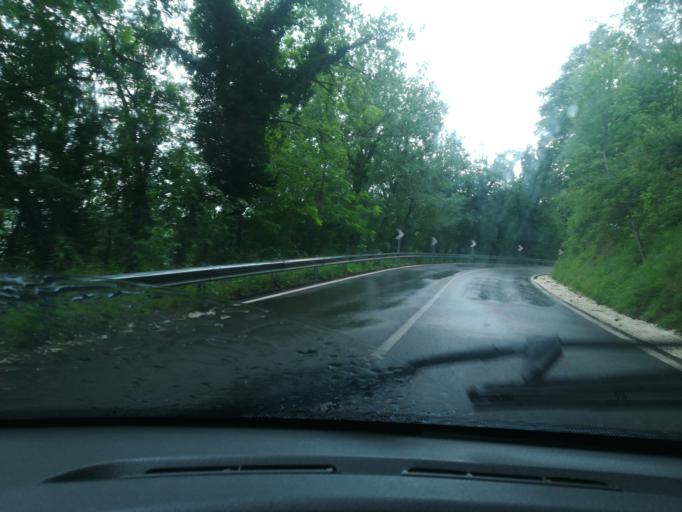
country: IT
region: The Marches
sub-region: Provincia di Macerata
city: Sarnano
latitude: 43.0144
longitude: 13.3270
